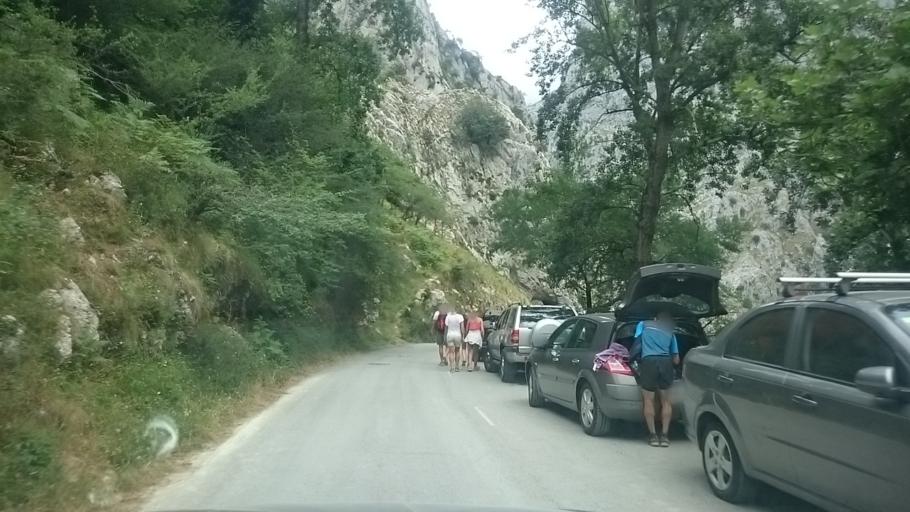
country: ES
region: Asturias
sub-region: Province of Asturias
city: Carrena
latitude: 43.2548
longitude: -4.8366
